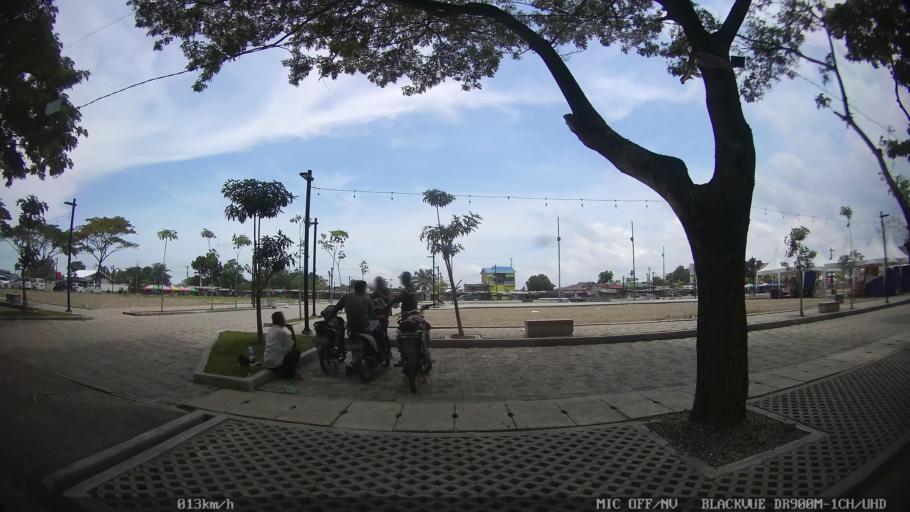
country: ID
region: North Sumatra
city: Labuhan Deli
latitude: 3.6927
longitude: 98.6941
